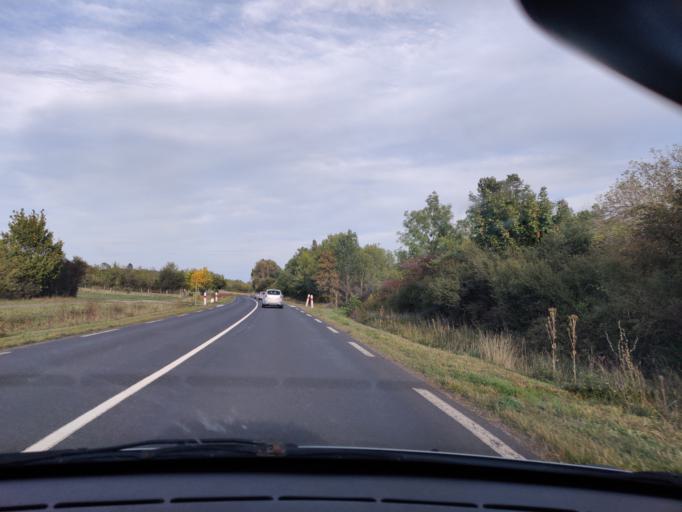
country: FR
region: Auvergne
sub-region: Departement du Puy-de-Dome
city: Mozac
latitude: 45.8996
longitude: 3.0851
